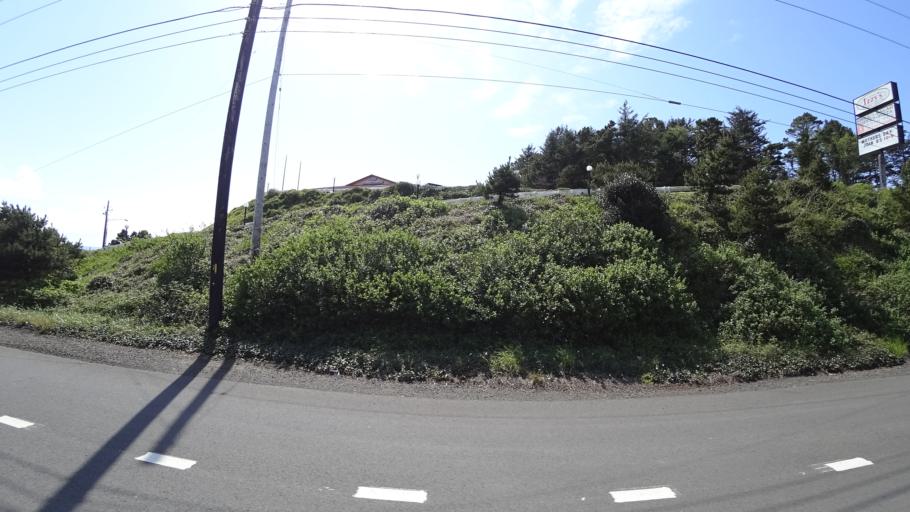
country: US
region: Oregon
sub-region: Lincoln County
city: Newport
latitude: 44.6759
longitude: -124.0607
